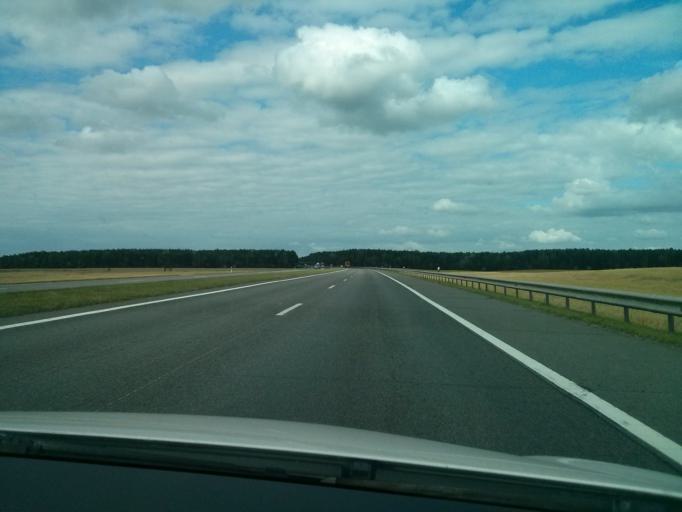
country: BY
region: Minsk
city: Zamostochcha
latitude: 53.8823
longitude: 27.9360
